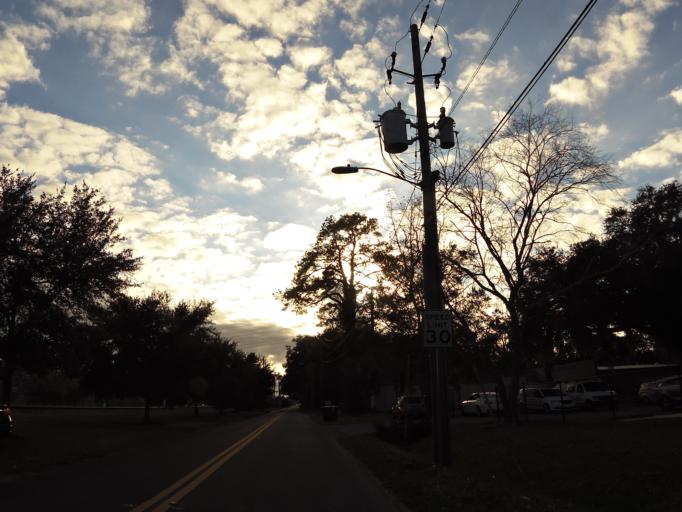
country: US
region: Florida
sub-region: Duval County
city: Jacksonville
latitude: 30.3127
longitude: -81.7063
